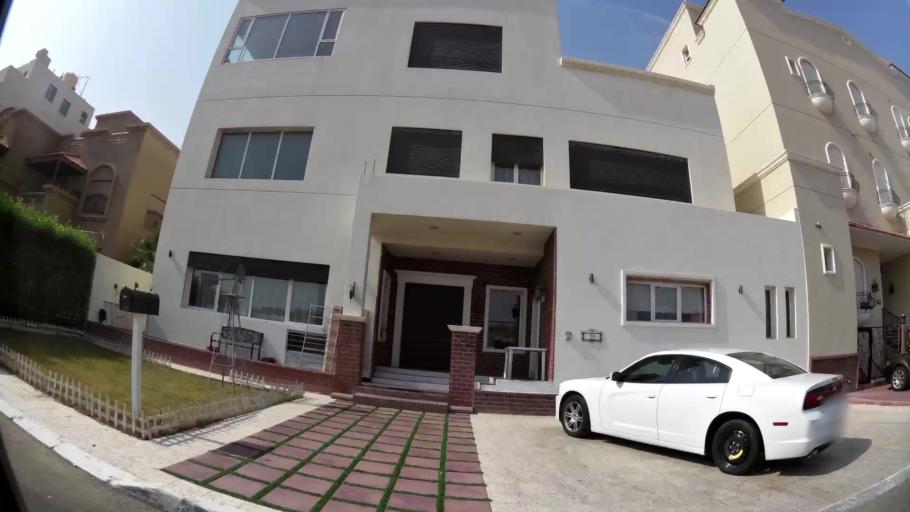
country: KW
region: Muhafazat al Jahra'
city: Al Jahra'
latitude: 29.3372
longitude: 47.7704
